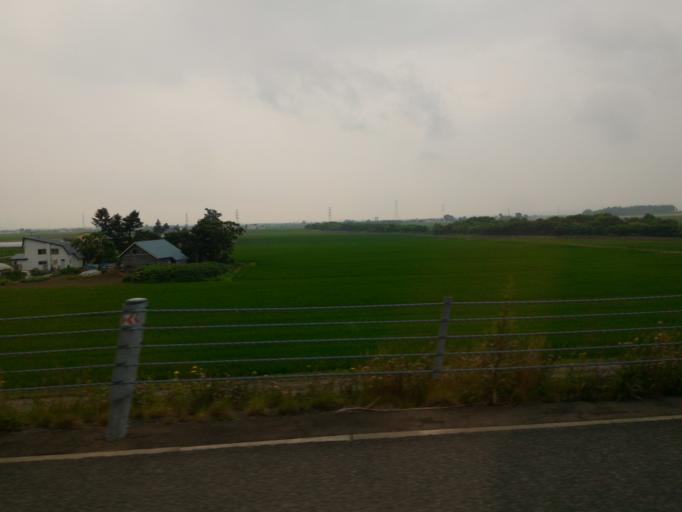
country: JP
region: Hokkaido
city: Fukagawa
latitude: 43.8011
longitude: 141.9123
